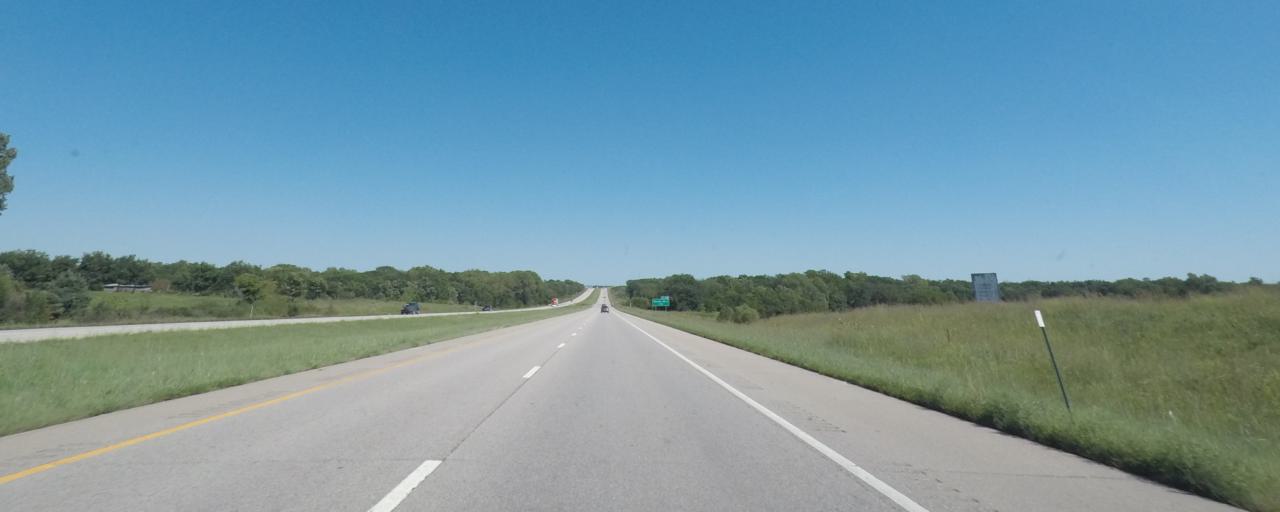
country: US
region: Kansas
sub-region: Lyon County
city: Emporia
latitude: 38.4112
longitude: -96.0660
